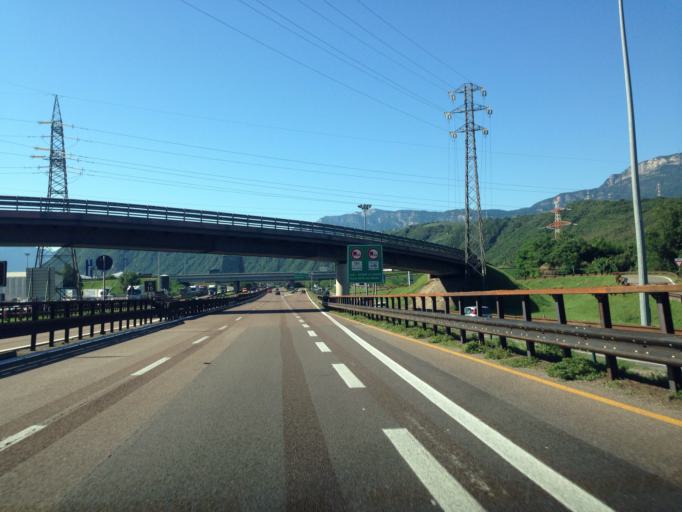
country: IT
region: Trentino-Alto Adige
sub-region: Bolzano
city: Bolzano
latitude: 46.4780
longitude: 11.3188
